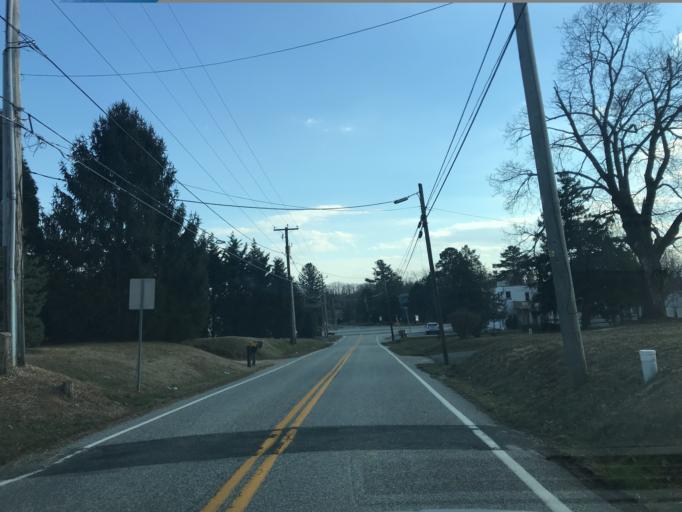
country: US
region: Maryland
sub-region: Cecil County
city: North East
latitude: 39.6427
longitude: -75.9616
